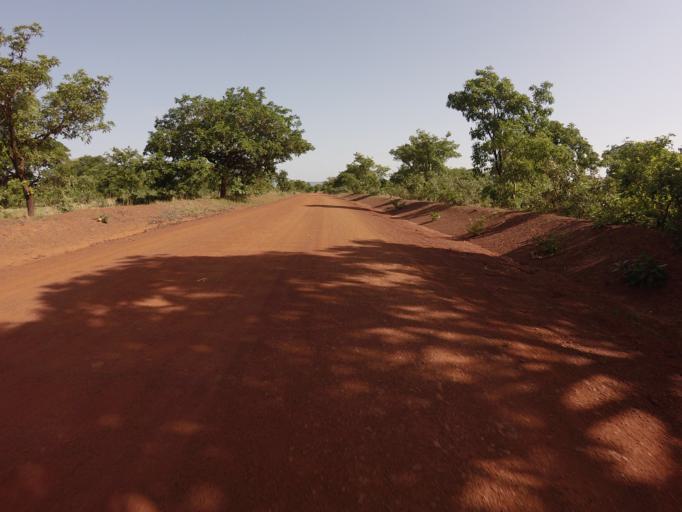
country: GH
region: Upper East
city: Bawku
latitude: 10.7484
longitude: -0.2002
